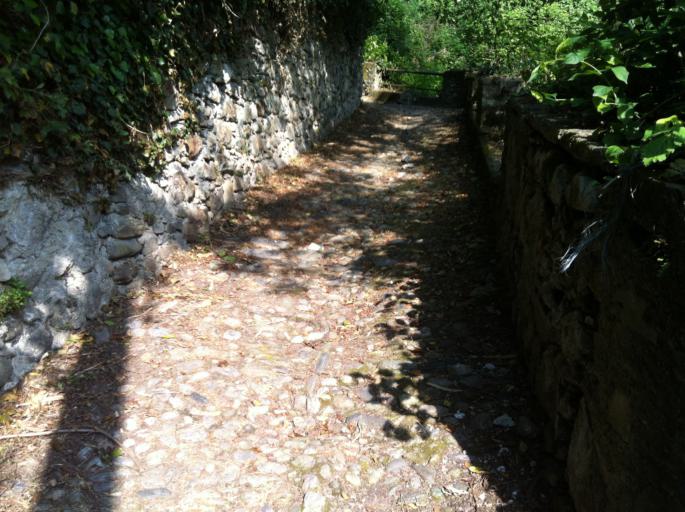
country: IT
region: Lombardy
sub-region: Provincia di Como
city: Menaggio
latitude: 46.0240
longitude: 9.2323
